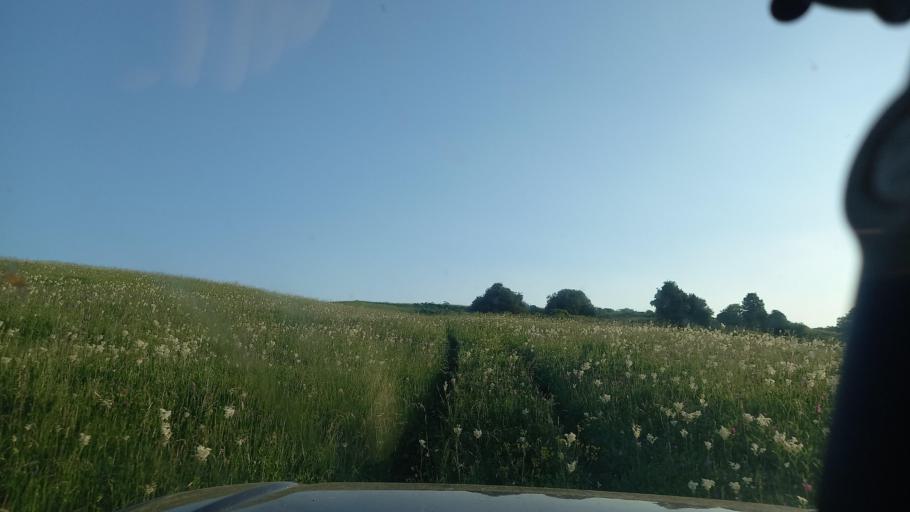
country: RU
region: Karachayevo-Cherkesiya
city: Kurdzhinovo
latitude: 44.1294
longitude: 41.0926
